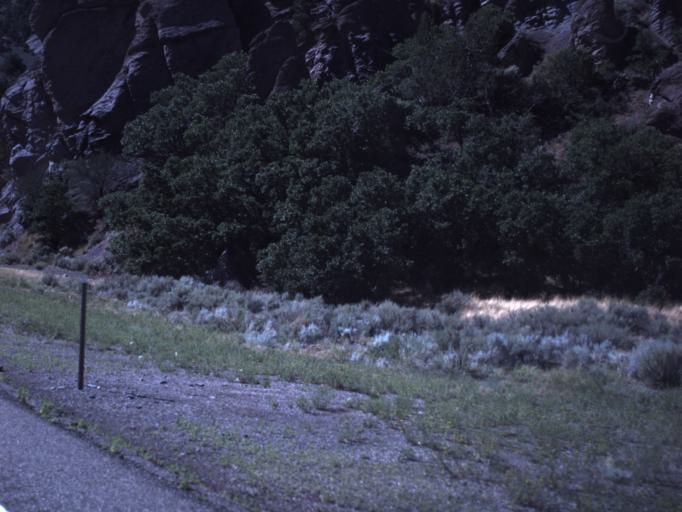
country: US
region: Utah
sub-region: Sevier County
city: Monroe
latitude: 38.5395
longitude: -112.2671
